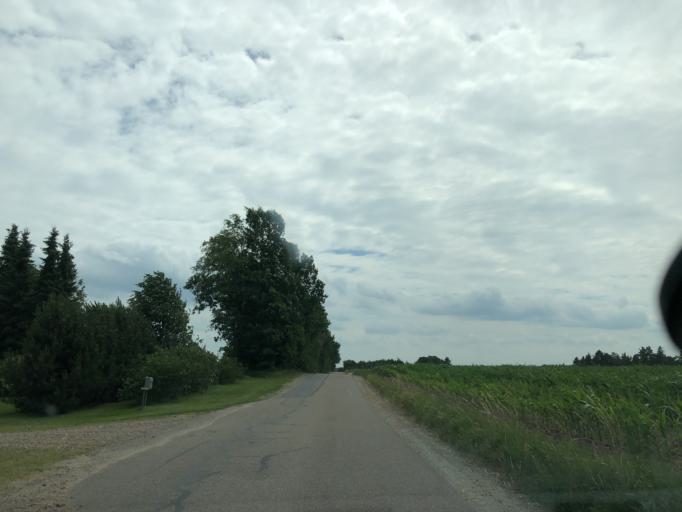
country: DK
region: Central Jutland
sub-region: Silkeborg Kommune
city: Svejbaek
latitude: 56.2073
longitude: 9.6880
